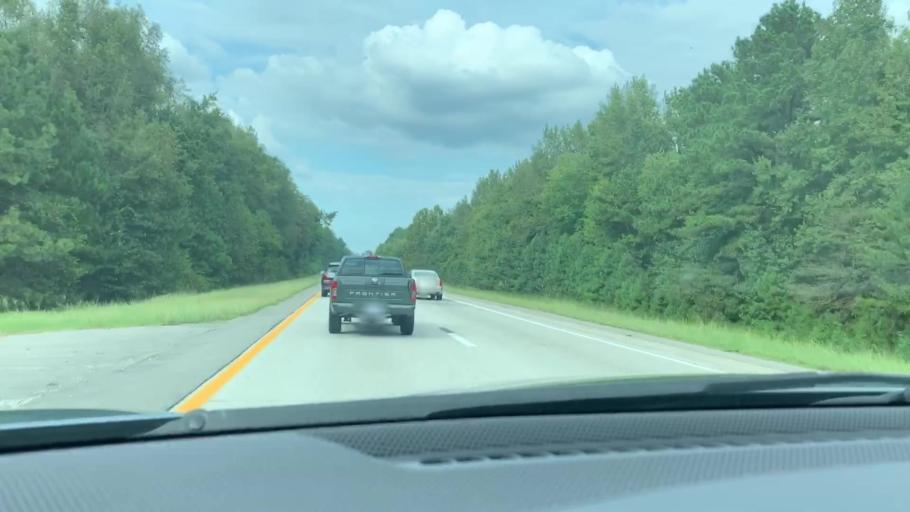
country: US
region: South Carolina
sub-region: Dorchester County
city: Saint George
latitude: 33.1189
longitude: -80.6414
